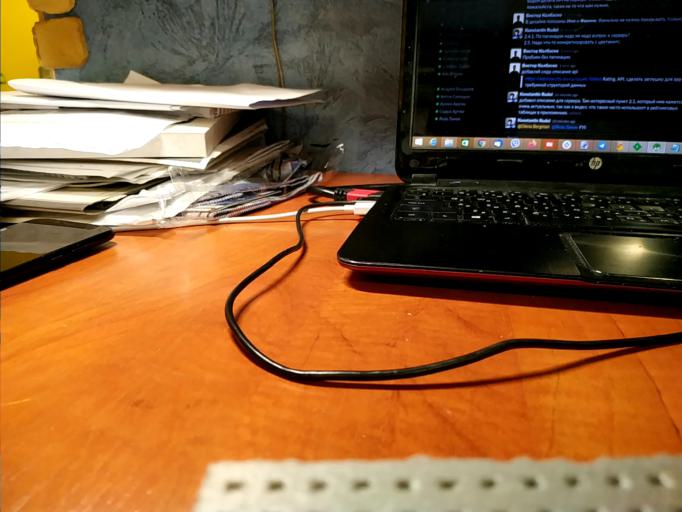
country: RU
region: Tverskaya
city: Spirovo
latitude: 57.4518
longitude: 34.9162
